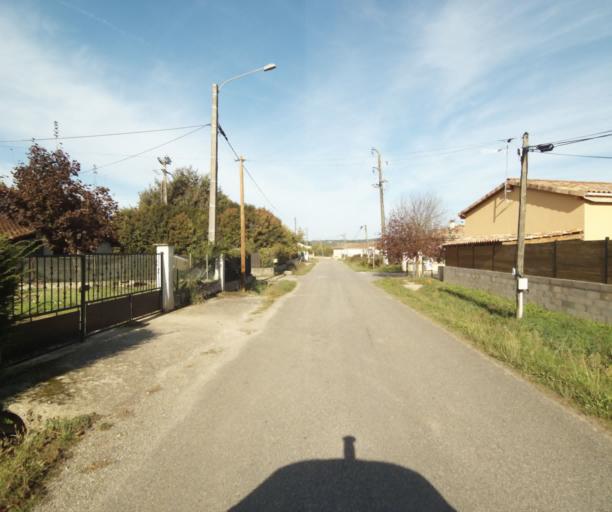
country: FR
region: Midi-Pyrenees
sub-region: Departement du Tarn-et-Garonne
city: Nohic
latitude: 43.9101
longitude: 1.4463
